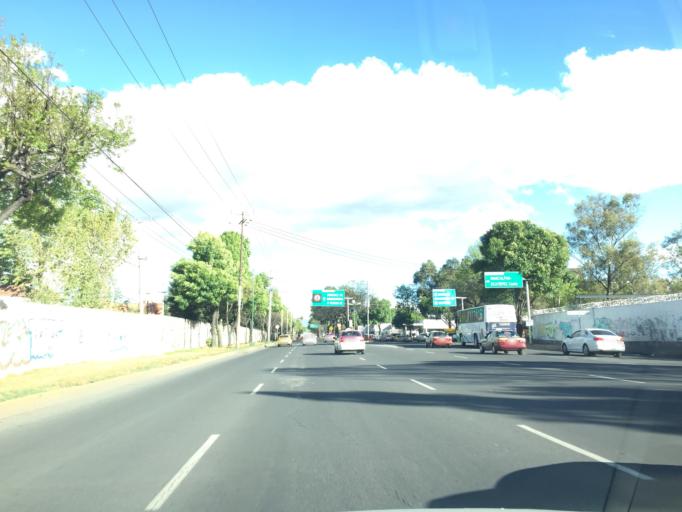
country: MX
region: Mexico
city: Colonia Lindavista
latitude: 19.4860
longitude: -99.1400
